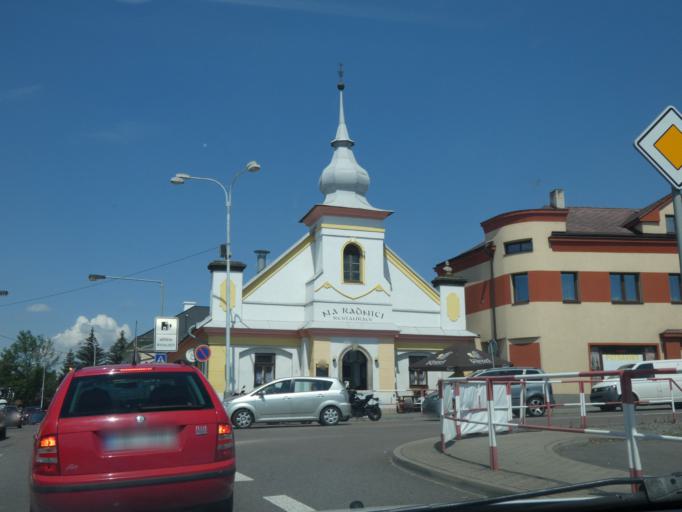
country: CZ
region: Pardubicky
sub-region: Okres Chrudim
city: Nasavrky
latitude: 49.7866
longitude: 15.8160
